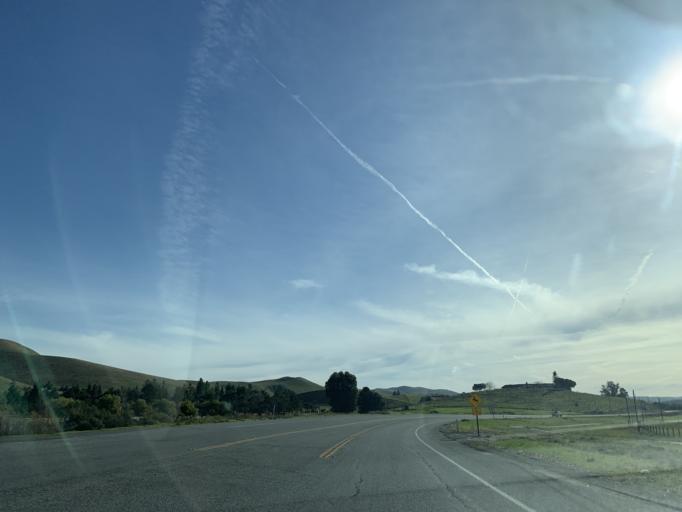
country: US
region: California
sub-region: San Benito County
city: Ridgemark
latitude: 36.7951
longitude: -121.3272
